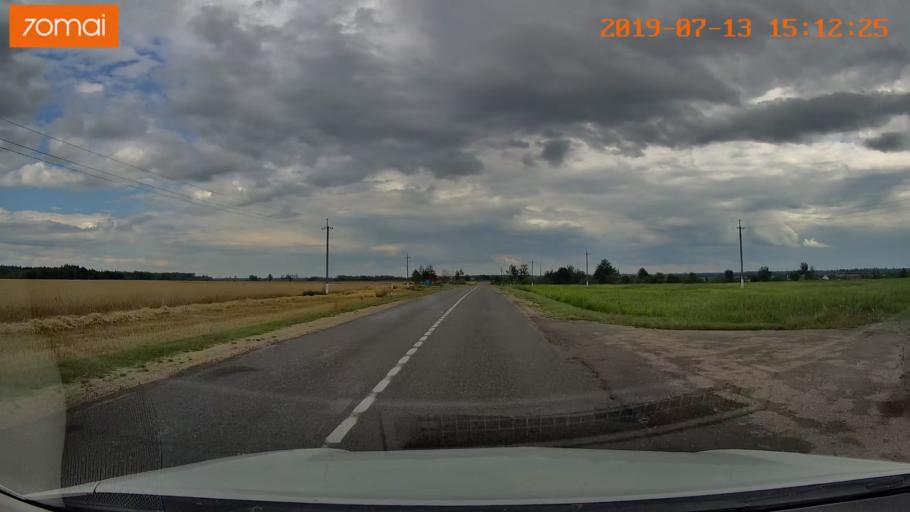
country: BY
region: Mogilev
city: Hlusha
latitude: 53.1488
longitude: 28.7914
